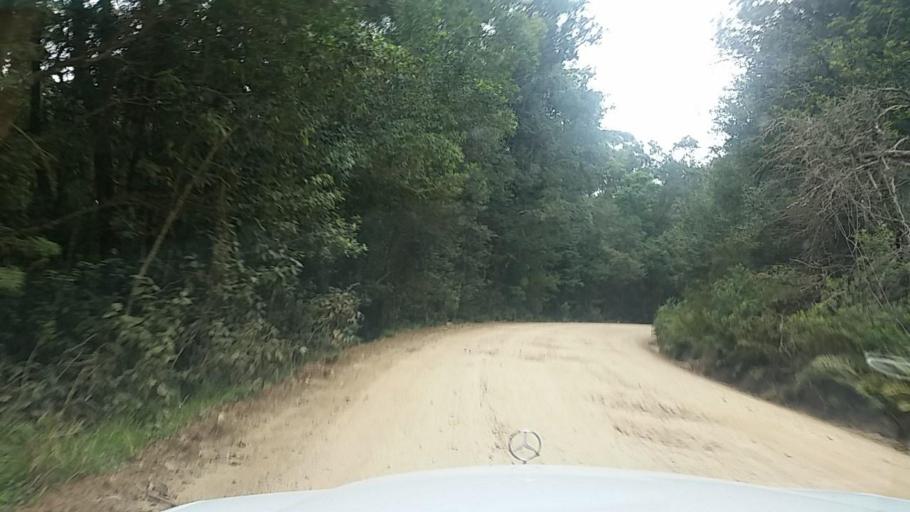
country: ZA
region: Western Cape
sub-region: Eden District Municipality
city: Knysna
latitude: -33.9394
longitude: 23.1606
